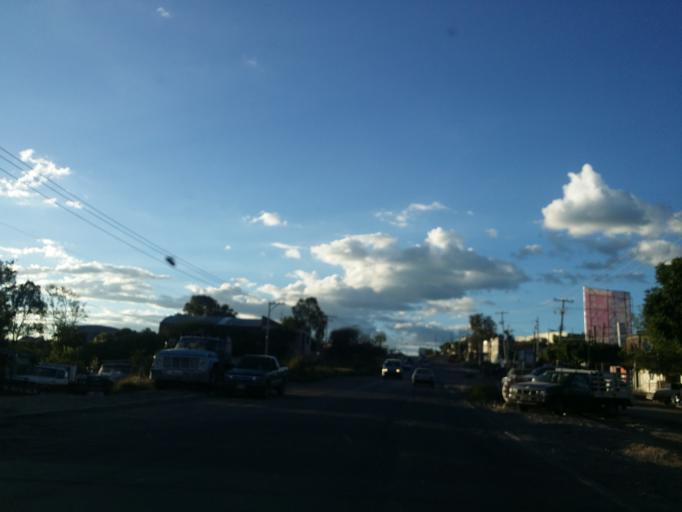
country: MX
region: Guanajuato
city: Leon
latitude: 21.2024
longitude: -101.6750
